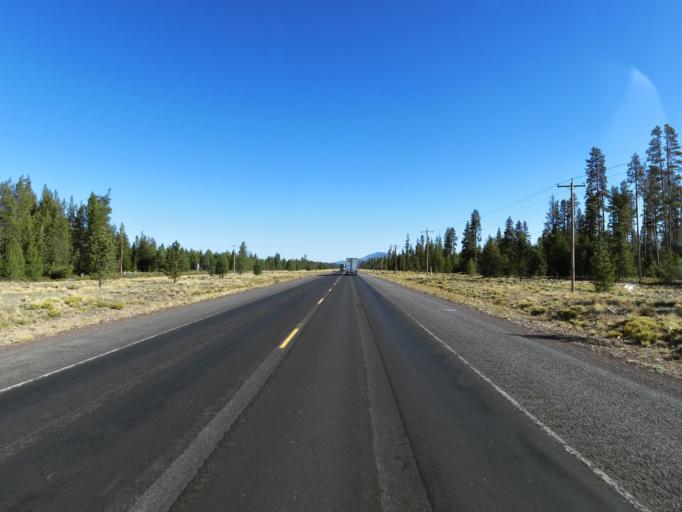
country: US
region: Oregon
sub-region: Deschutes County
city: La Pine
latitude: 43.1448
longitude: -121.7985
